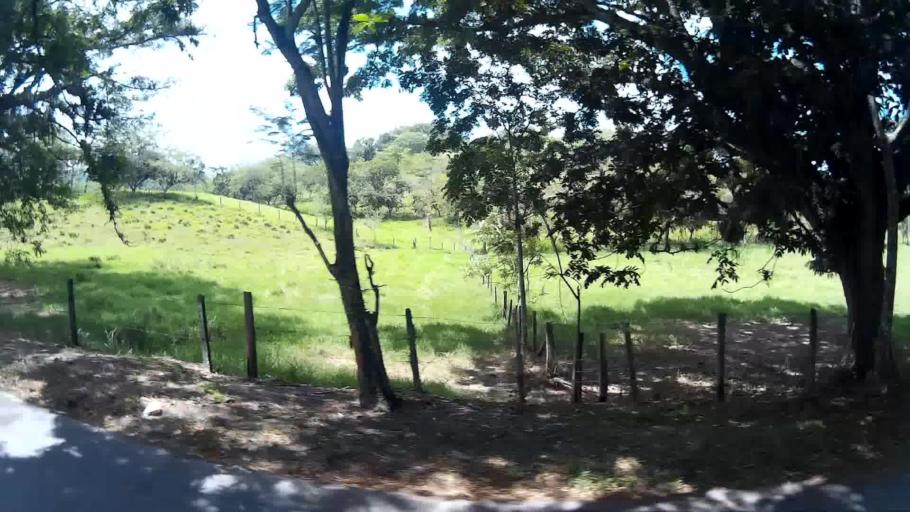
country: CO
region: Risaralda
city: La Virginia
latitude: 4.9003
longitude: -75.8690
